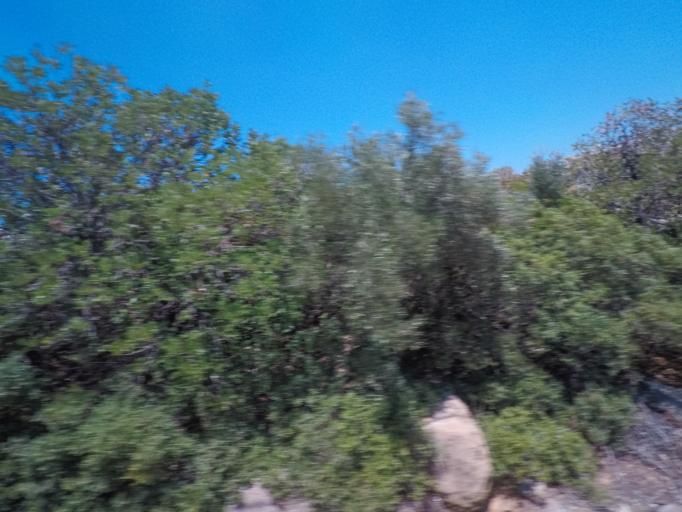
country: GR
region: Crete
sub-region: Nomos Lasithiou
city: Skhisma
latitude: 35.2418
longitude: 25.7272
